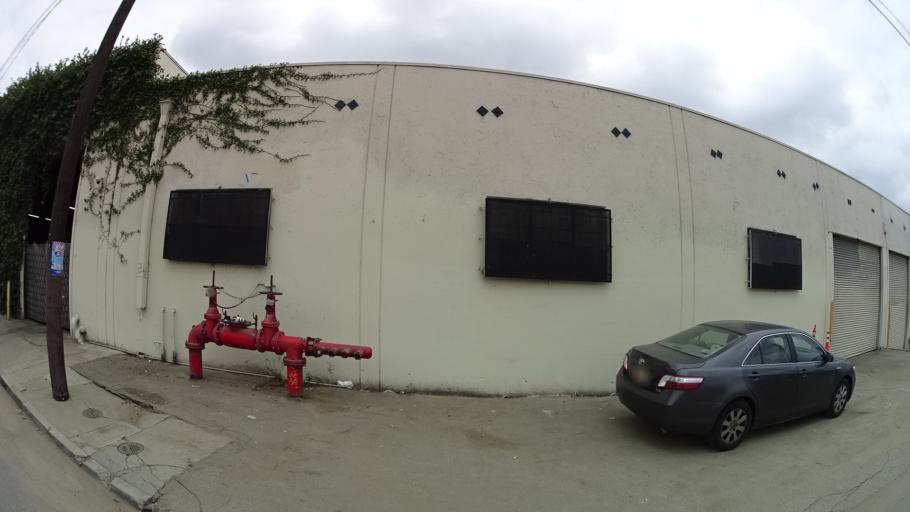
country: US
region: California
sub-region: Los Angeles County
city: Belvedere
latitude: 34.0618
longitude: -118.1855
